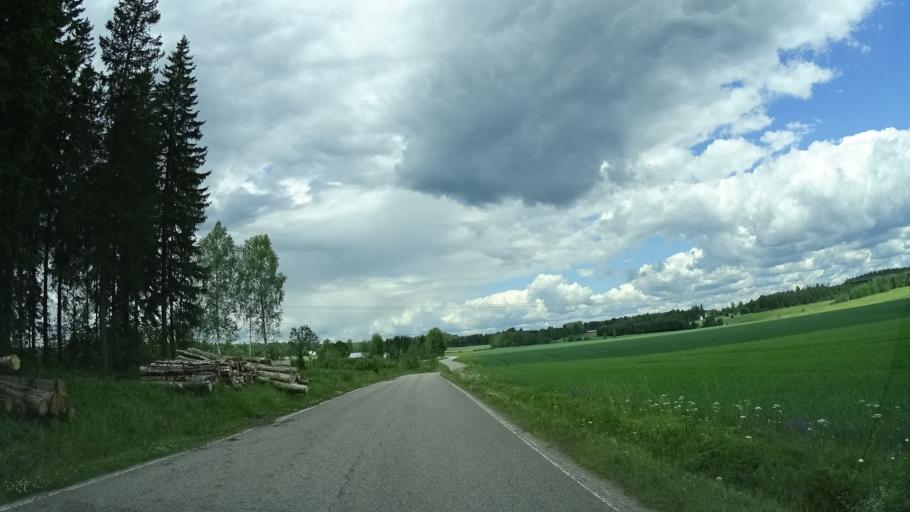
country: FI
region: Uusimaa
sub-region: Helsinki
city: Vihti
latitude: 60.4222
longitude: 24.5347
